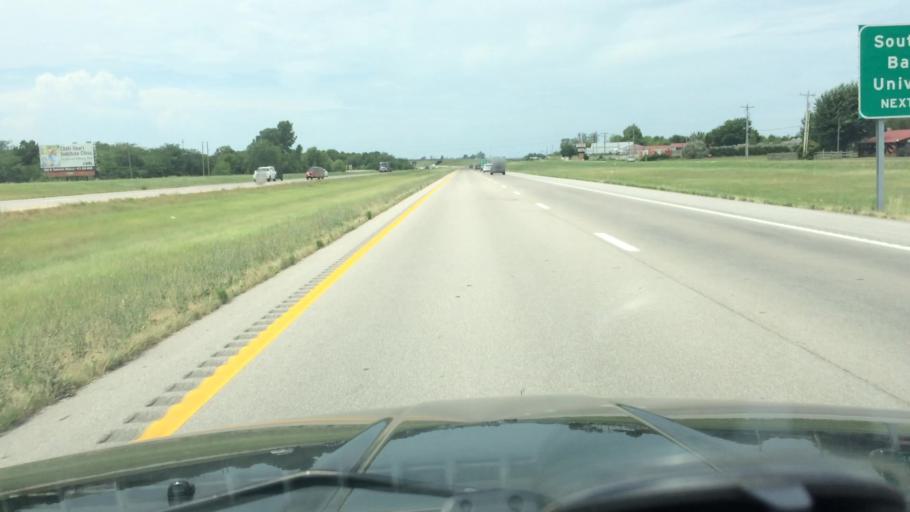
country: US
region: Missouri
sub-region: Polk County
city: Bolivar
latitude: 37.5657
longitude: -93.3941
